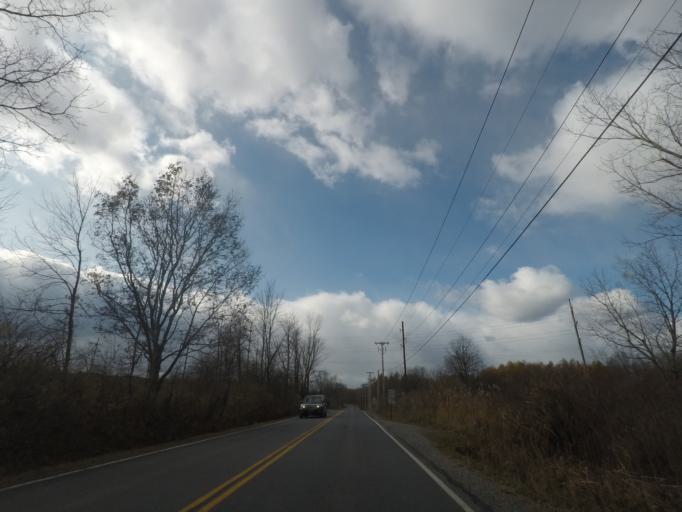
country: US
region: New York
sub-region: Saratoga County
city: Ballston Spa
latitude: 42.9637
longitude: -73.8303
